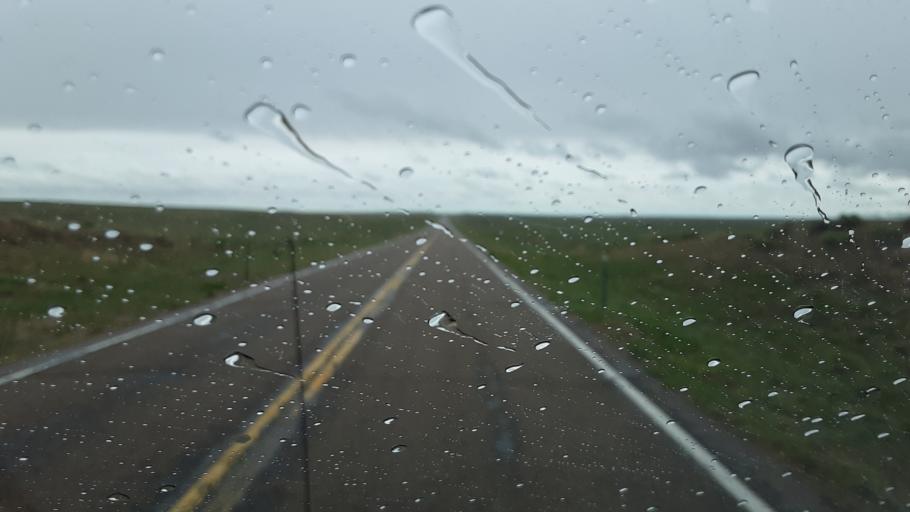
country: US
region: Colorado
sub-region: Lincoln County
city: Hugo
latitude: 38.8494
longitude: -103.2588
